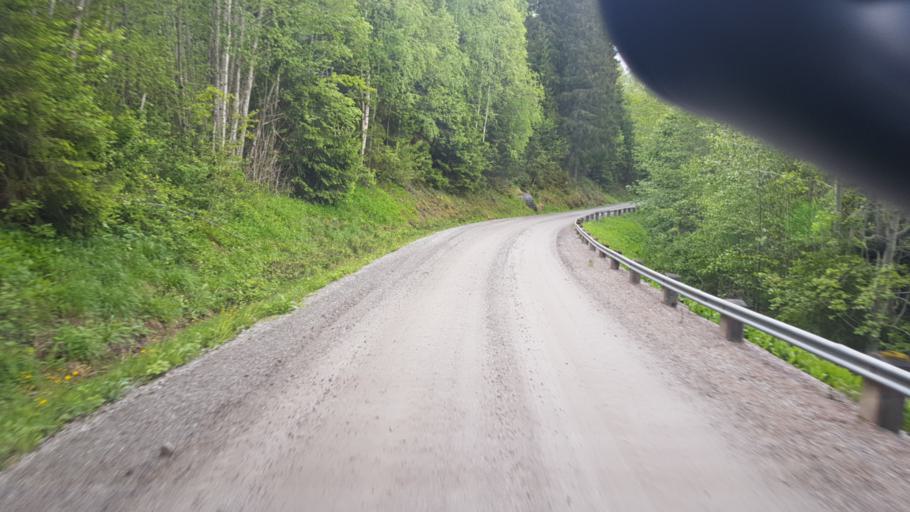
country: NO
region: Ostfold
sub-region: Romskog
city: Romskog
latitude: 59.7073
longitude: 11.9627
